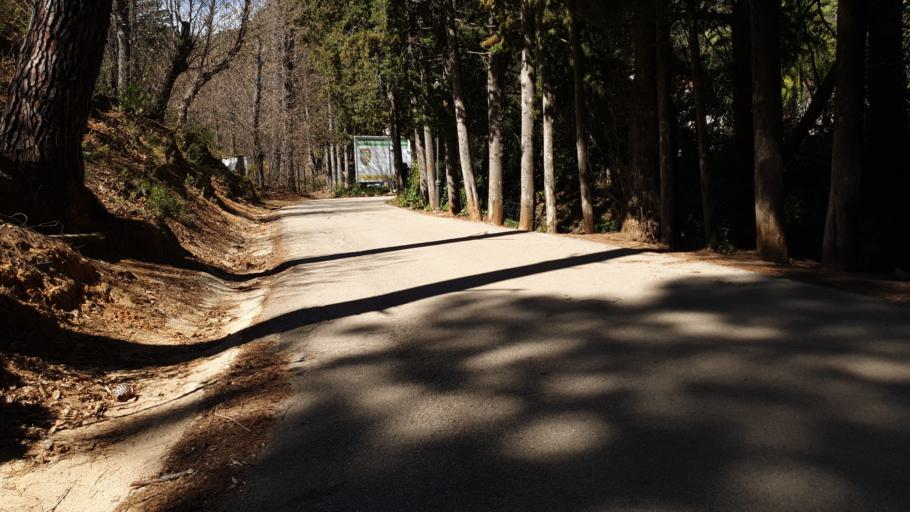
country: ES
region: Andalusia
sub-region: Provincia de Malaga
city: Ojen
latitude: 36.5796
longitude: -4.8850
